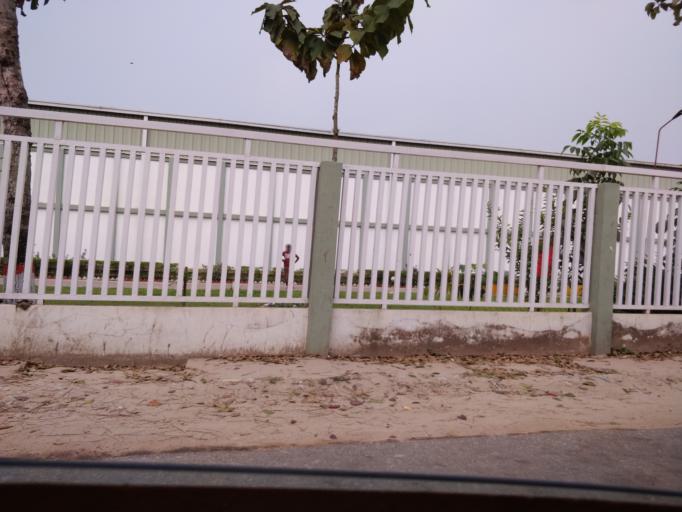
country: BD
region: Sylhet
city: Habiganj
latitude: 24.1715
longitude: 91.3553
